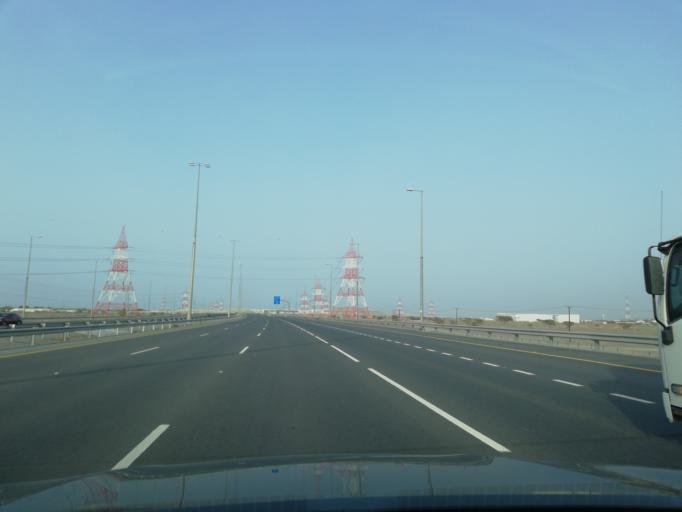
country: OM
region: Al Batinah
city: Barka'
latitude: 23.6304
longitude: 58.0154
